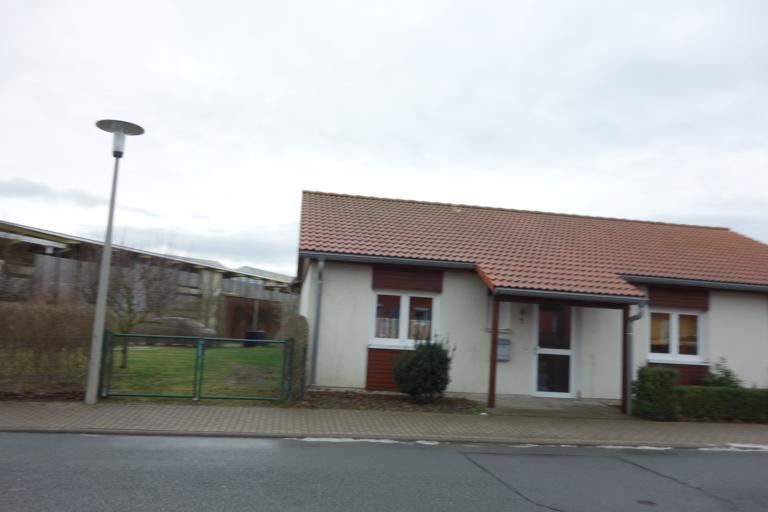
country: DE
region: Saxony
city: Freiberg
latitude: 50.9204
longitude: 13.3205
